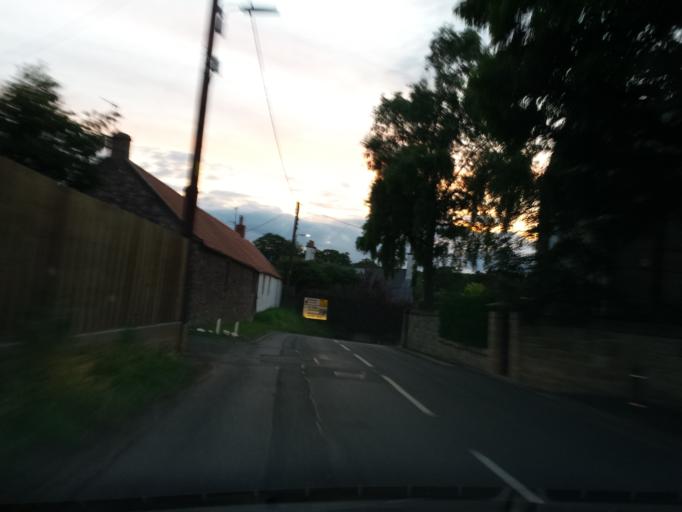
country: GB
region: Scotland
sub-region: The Scottish Borders
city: Eyemouth
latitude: 55.8851
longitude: -2.1571
